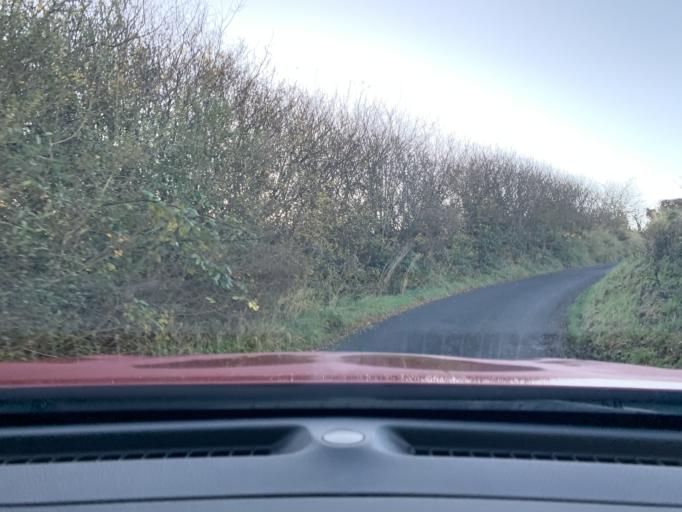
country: IE
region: Connaught
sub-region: Sligo
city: Ballymote
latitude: 54.0667
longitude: -8.5353
